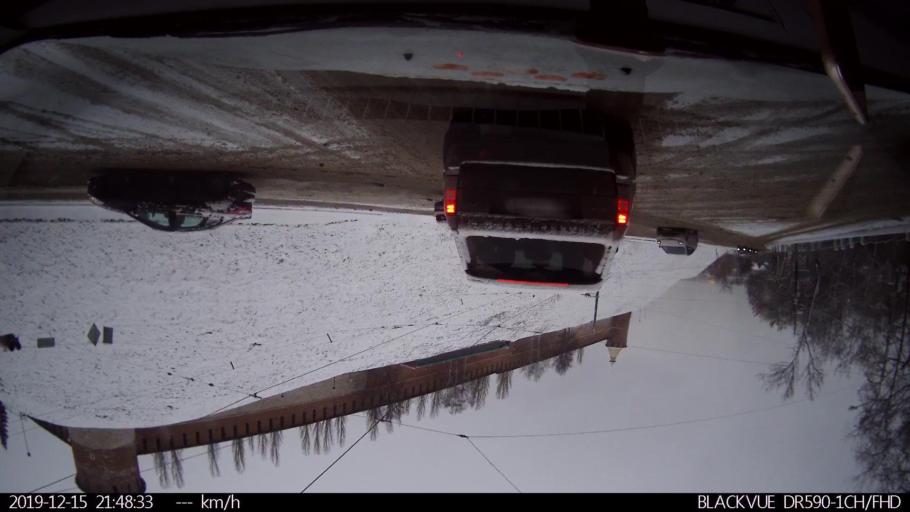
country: RU
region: Nizjnij Novgorod
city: Knyaginino
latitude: 55.8649
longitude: 45.0238
